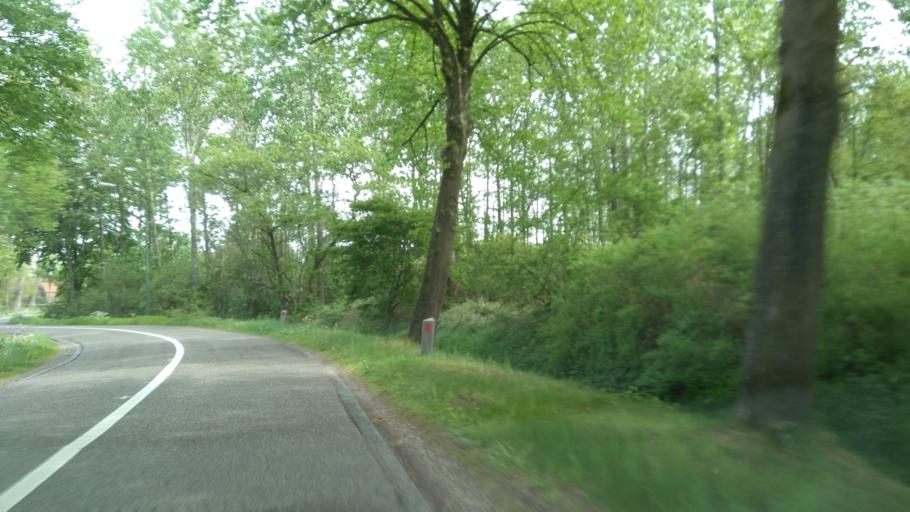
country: BE
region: Flanders
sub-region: Provincie Antwerpen
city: Baarle-Hertog
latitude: 51.4117
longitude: 4.9004
